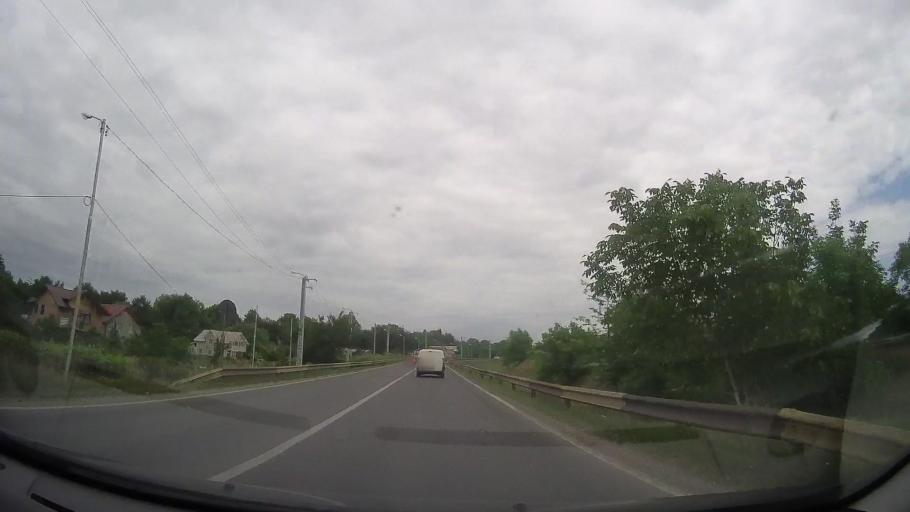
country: RO
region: Prahova
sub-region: Comuna Blejoiu
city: Blejoi
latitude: 44.9915
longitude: 26.0138
